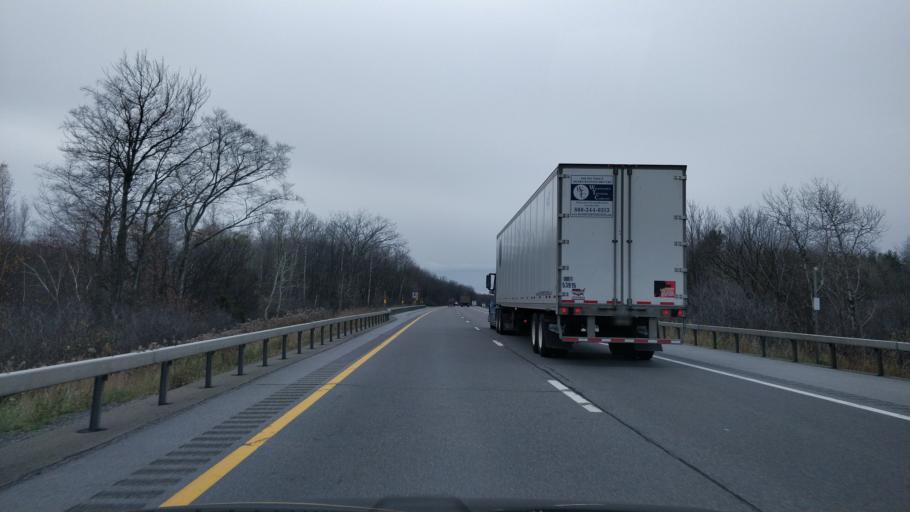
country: US
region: New York
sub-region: Oswego County
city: Pulaski
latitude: 43.6208
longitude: -76.0852
